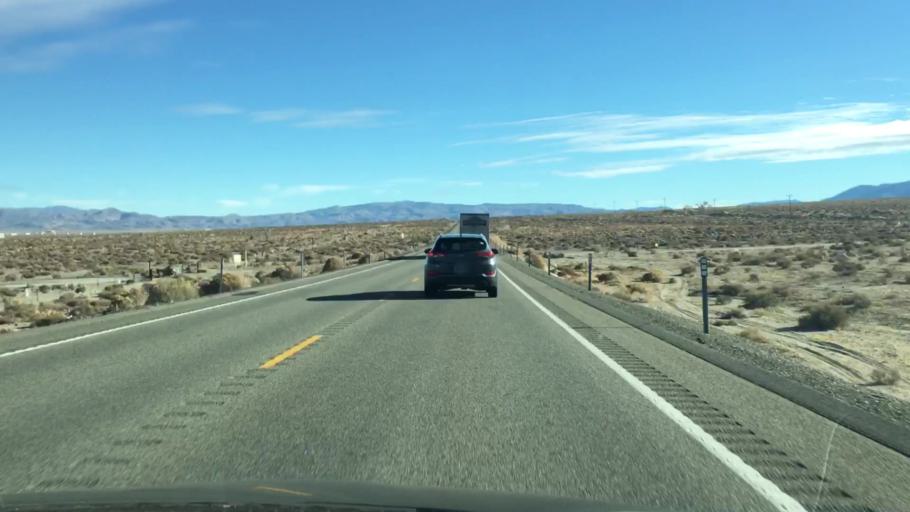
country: US
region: Nevada
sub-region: Mineral County
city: Hawthorne
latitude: 38.5741
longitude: -118.6958
